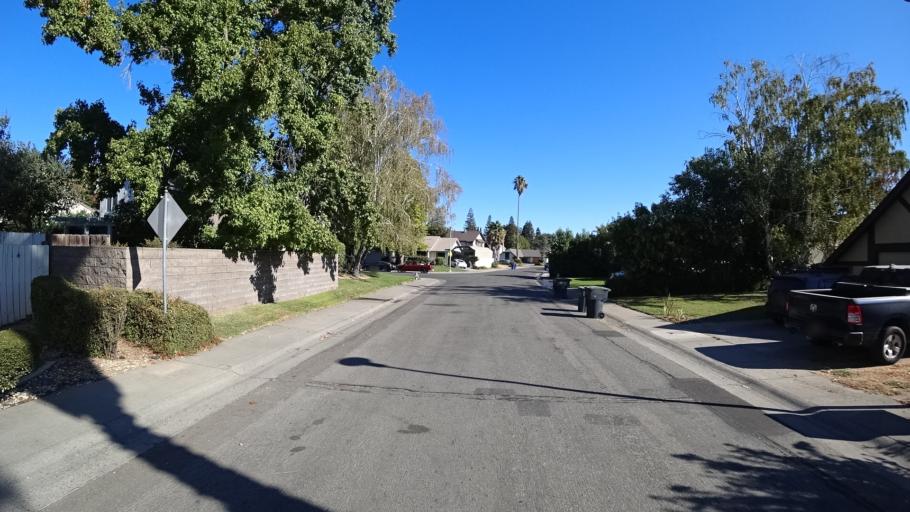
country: US
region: California
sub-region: Sacramento County
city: Florin
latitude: 38.4607
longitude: -121.4255
